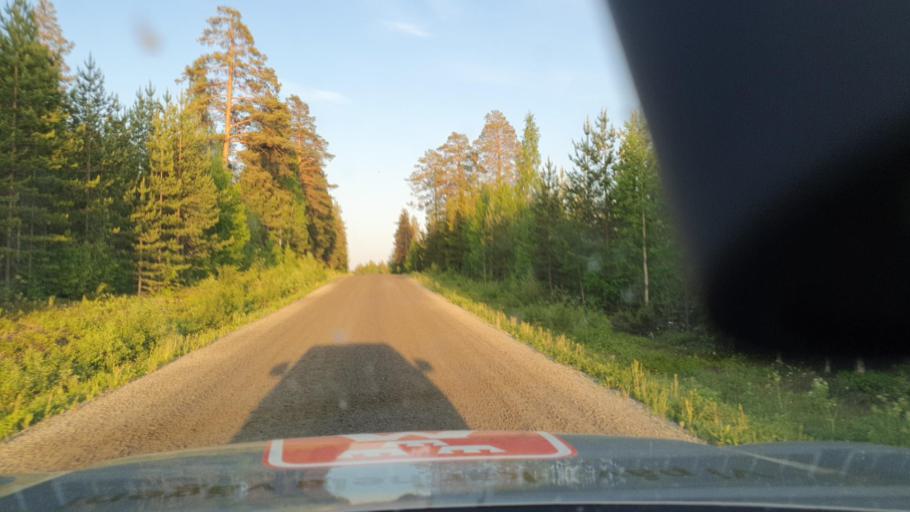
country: SE
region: Norrbotten
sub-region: Bodens Kommun
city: Boden
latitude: 66.0590
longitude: 21.7360
